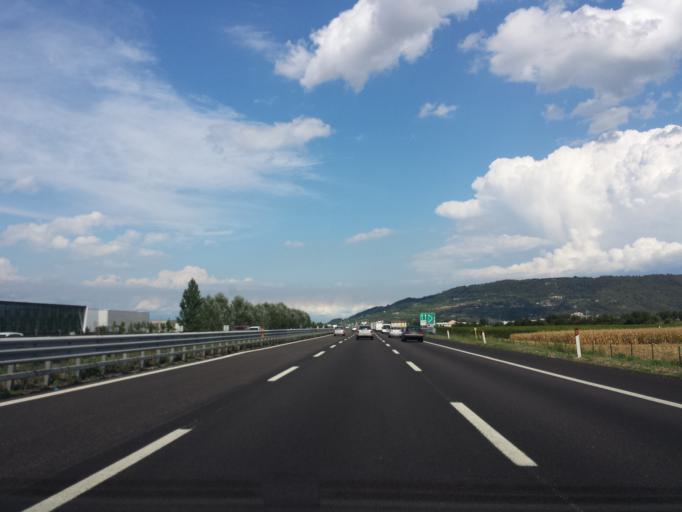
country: IT
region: Veneto
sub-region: Provincia di Vicenza
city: Brendola
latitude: 45.4678
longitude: 11.4135
